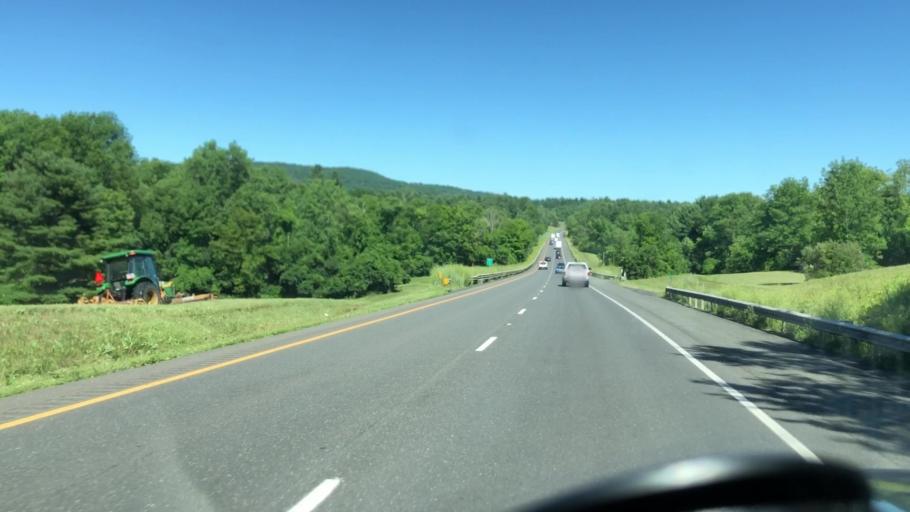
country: US
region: Massachusetts
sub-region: Berkshire County
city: Stockbridge
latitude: 42.3044
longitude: -73.3396
